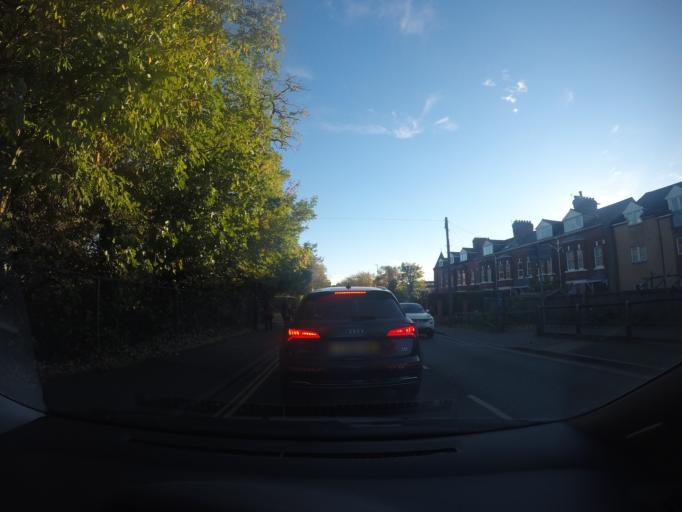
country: GB
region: England
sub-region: City of York
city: York
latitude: 53.9725
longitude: -1.0820
